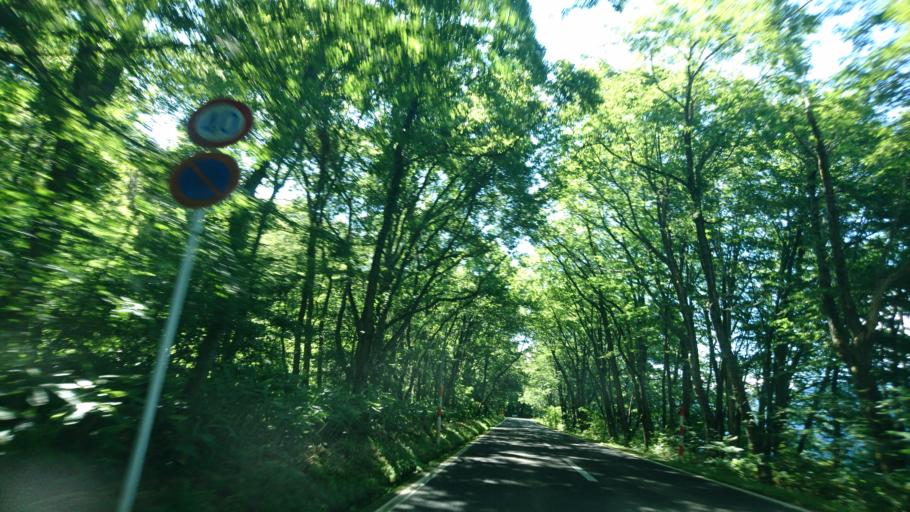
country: JP
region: Akita
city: Kakunodatemachi
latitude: 39.7464
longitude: 140.6810
